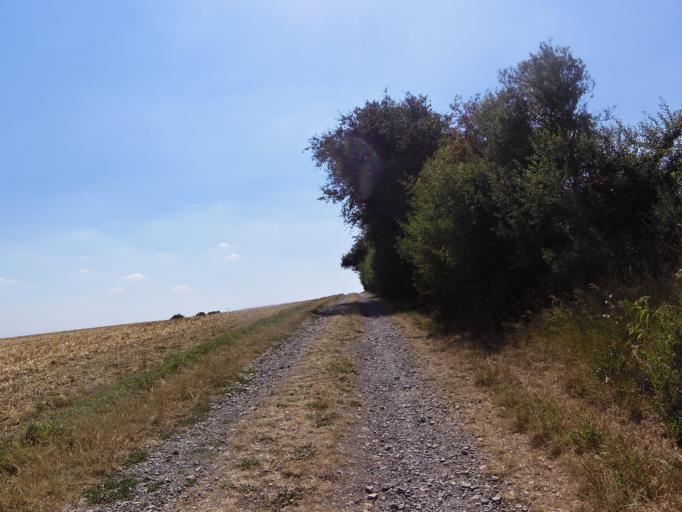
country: DE
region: Bavaria
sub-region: Regierungsbezirk Unterfranken
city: Wuerzburg
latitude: 49.8119
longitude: 9.9511
